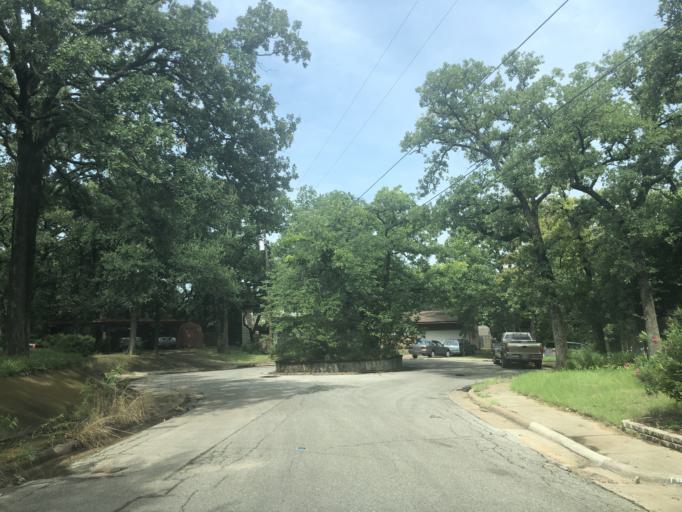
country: US
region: Texas
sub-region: Dallas County
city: Irving
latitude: 32.8048
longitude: -96.9671
